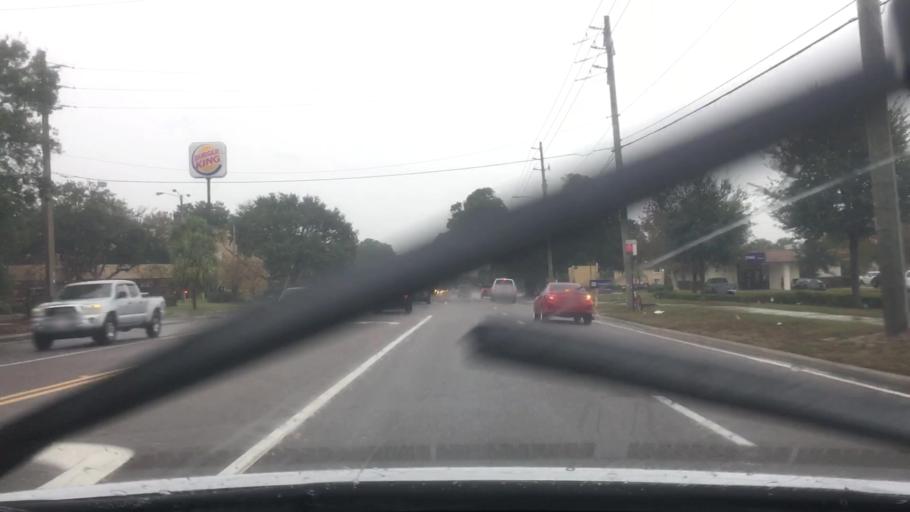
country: US
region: Florida
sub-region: Duval County
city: Jacksonville
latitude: 30.3249
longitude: -81.5468
